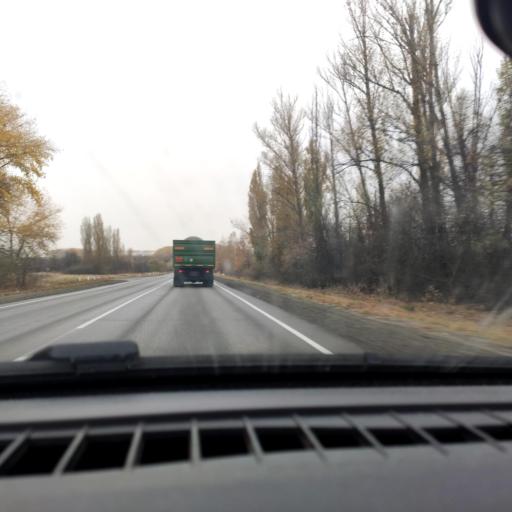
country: RU
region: Voronezj
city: Ostrogozhsk
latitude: 50.9683
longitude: 39.0072
